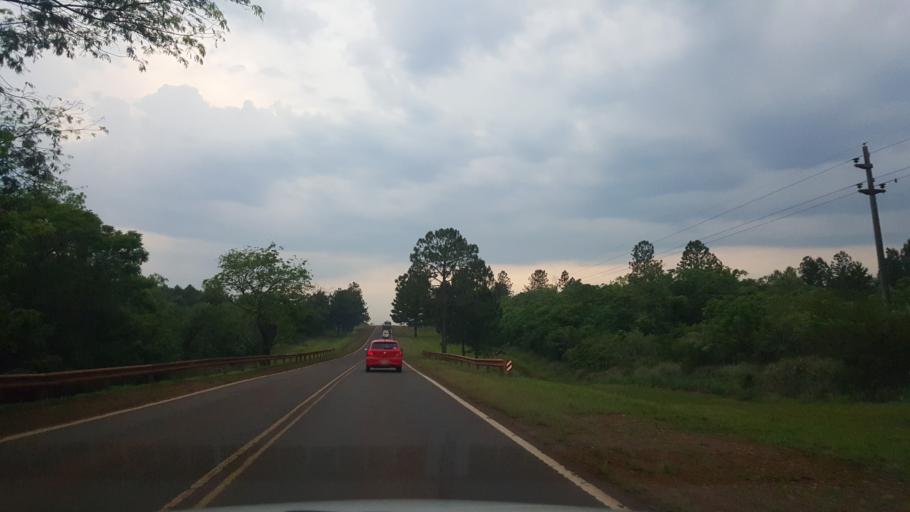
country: AR
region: Misiones
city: Gobernador Roca
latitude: -27.1688
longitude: -55.4447
